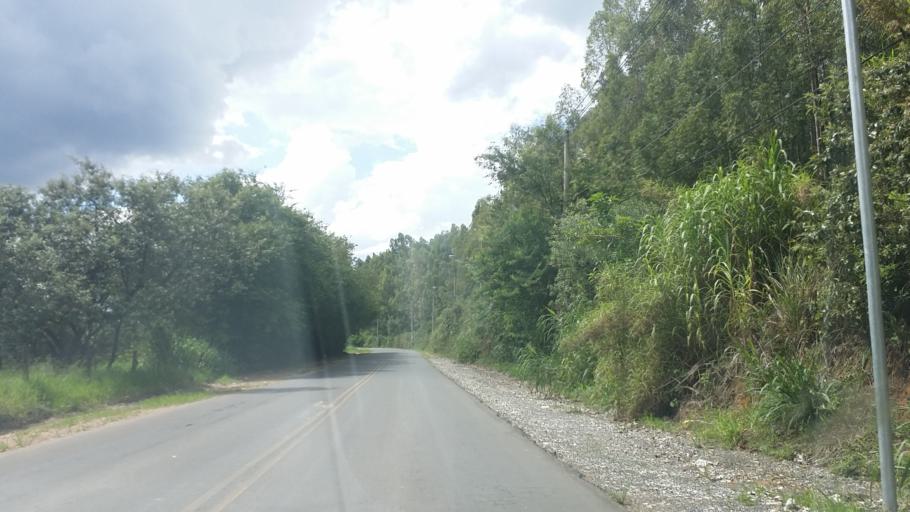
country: BR
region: Sao Paulo
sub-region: Itupeva
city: Itupeva
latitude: -23.1557
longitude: -47.1459
